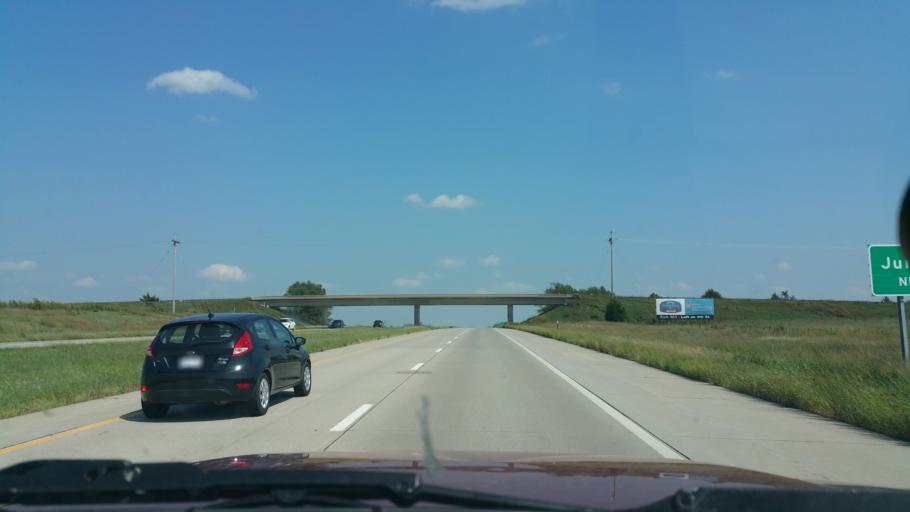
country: US
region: Kansas
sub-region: Geary County
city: Junction City
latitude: 39.0006
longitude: -96.9023
